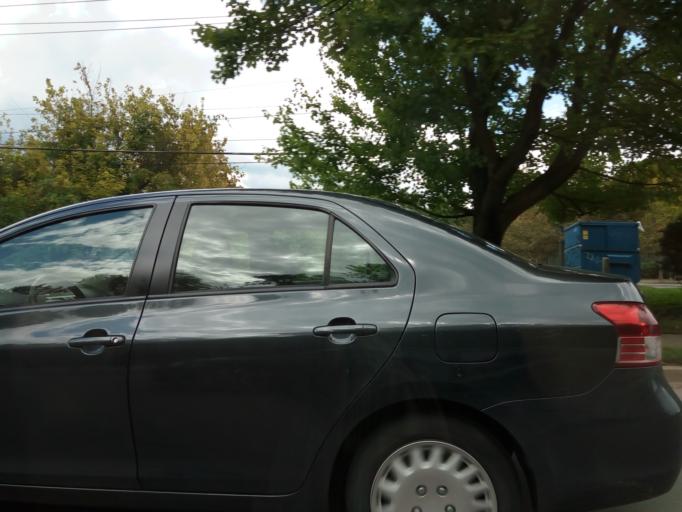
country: US
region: Kentucky
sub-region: Jefferson County
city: Audubon Park
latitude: 38.2062
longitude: -85.7135
